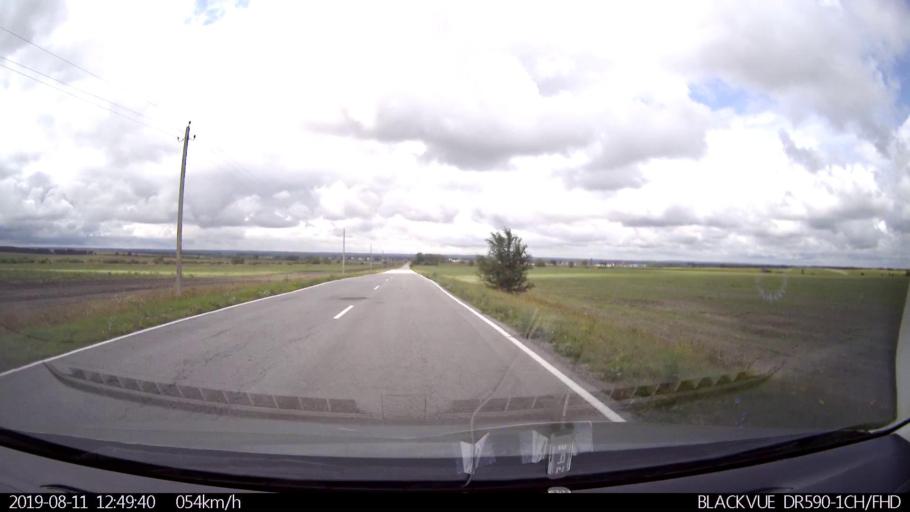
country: RU
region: Ulyanovsk
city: Ignatovka
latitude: 53.8750
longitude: 47.6834
